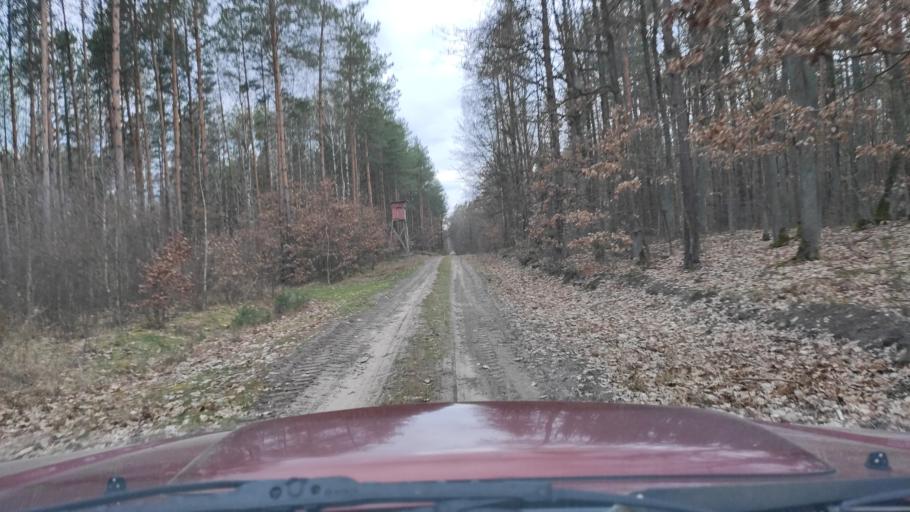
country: PL
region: Masovian Voivodeship
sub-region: Powiat kozienicki
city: Garbatka-Letnisko
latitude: 51.5083
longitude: 21.5505
